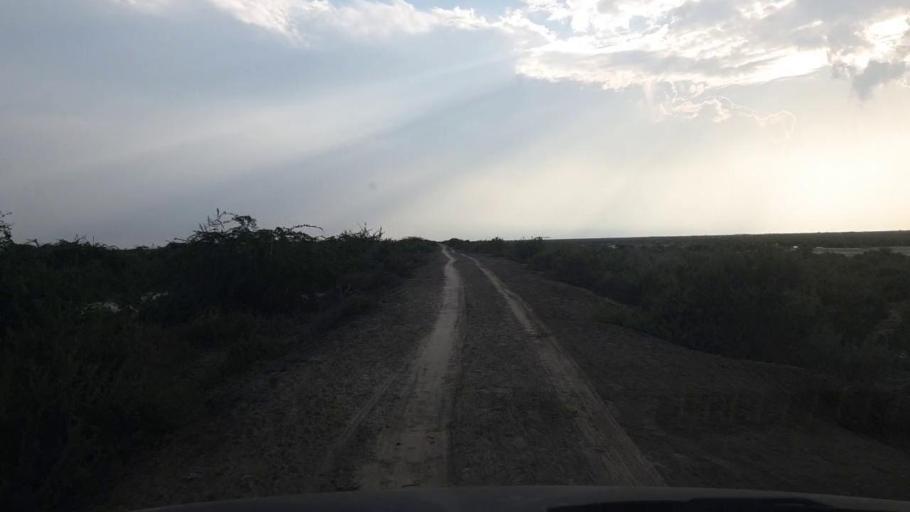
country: PK
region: Sindh
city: Badin
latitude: 24.4449
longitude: 68.6787
